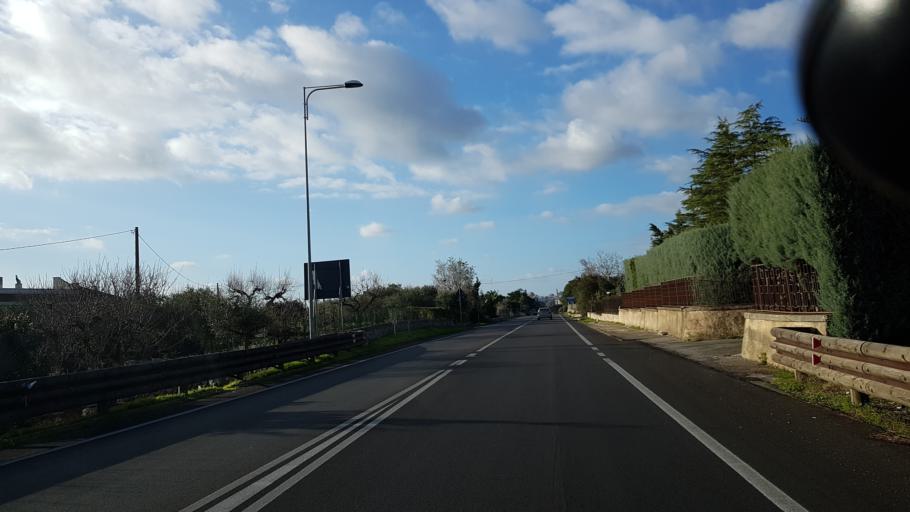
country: IT
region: Apulia
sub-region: Provincia di Bari
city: Putignano
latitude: 40.8408
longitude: 17.1475
